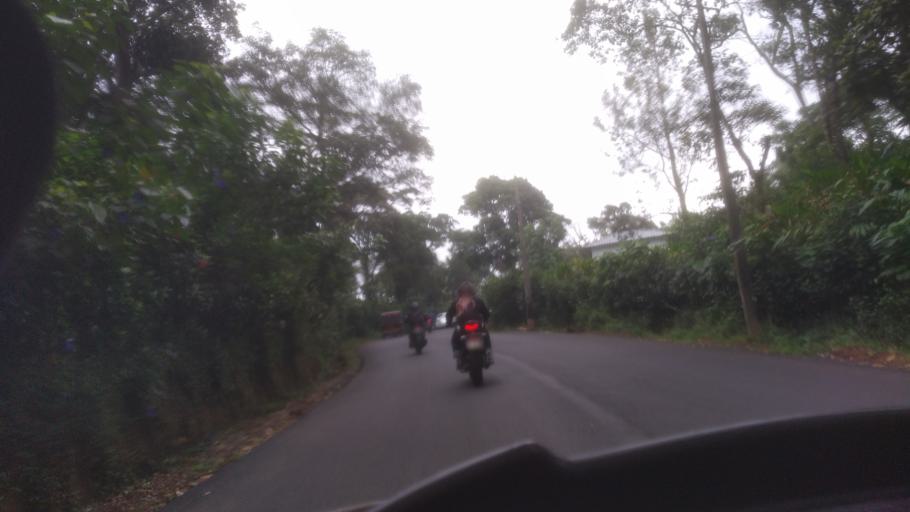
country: IN
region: Tamil Nadu
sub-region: Theni
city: Kombai
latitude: 9.8909
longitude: 77.1523
